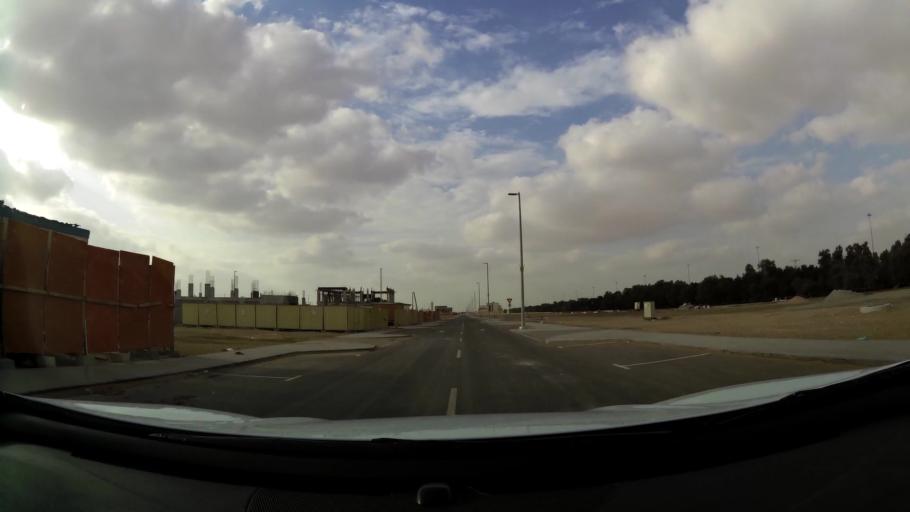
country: AE
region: Abu Dhabi
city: Abu Dhabi
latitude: 24.3375
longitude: 54.5767
